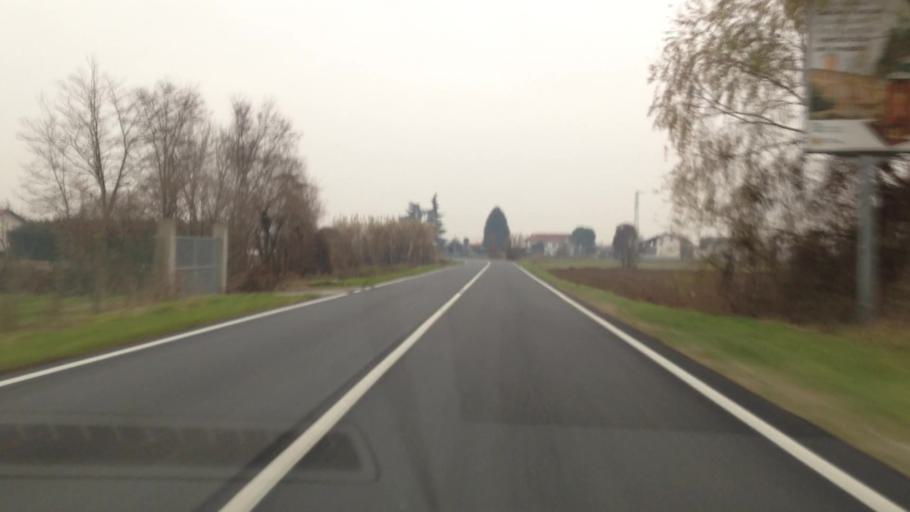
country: IT
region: Piedmont
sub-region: Provincia di Vercelli
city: Livorno Ferraris
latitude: 45.2856
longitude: 8.0623
